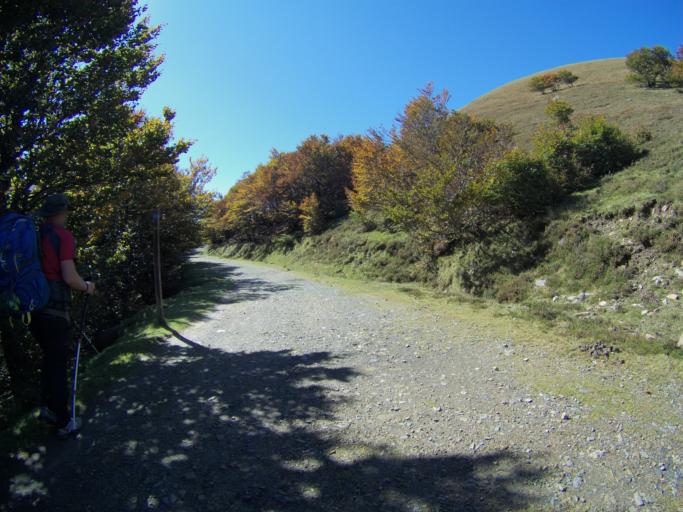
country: ES
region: Navarre
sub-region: Provincia de Navarra
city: Orbara
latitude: 43.0340
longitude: -1.2918
